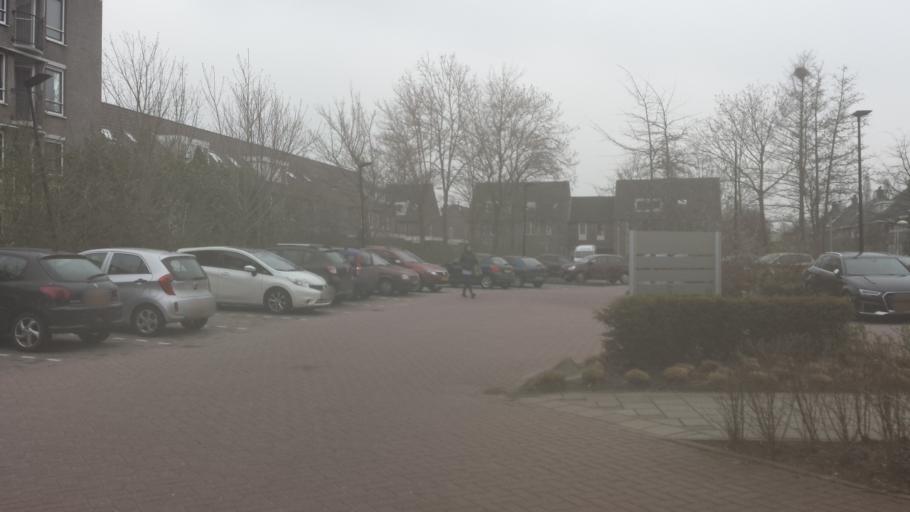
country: NL
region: South Holland
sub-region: Gemeente Gouda
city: Gouda
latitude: 52.0275
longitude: 4.7086
